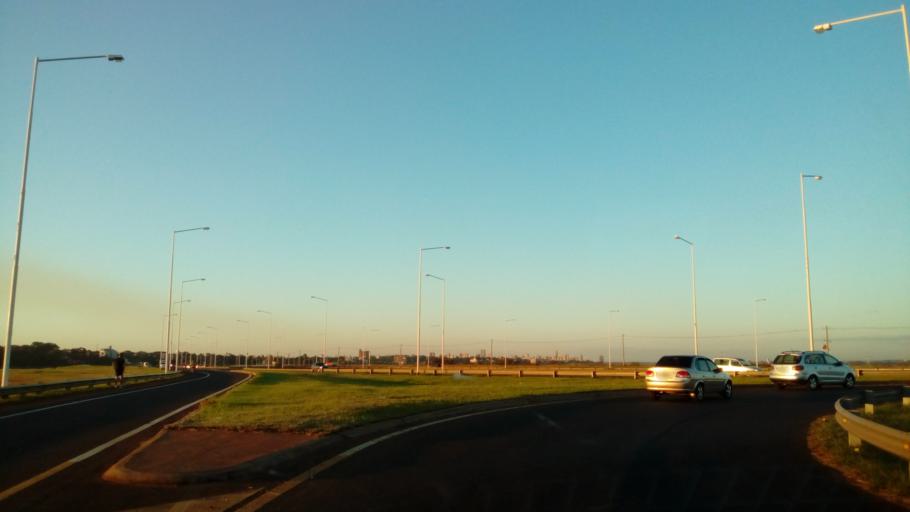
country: AR
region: Misiones
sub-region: Departamento de Capital
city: Posadas
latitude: -27.4148
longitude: -55.8877
